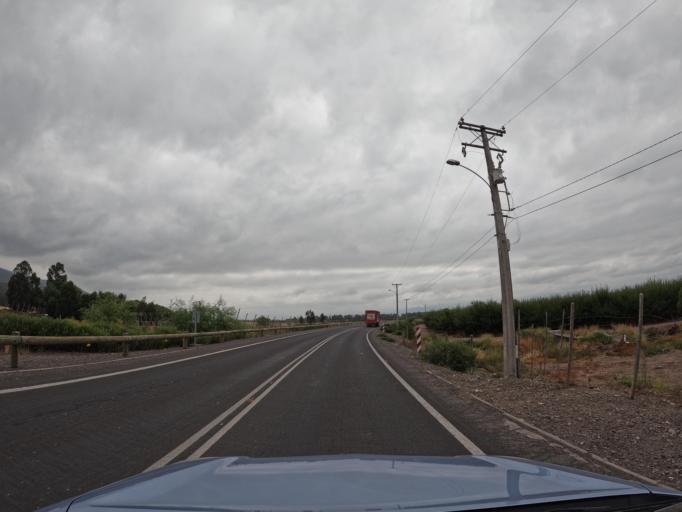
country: CL
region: O'Higgins
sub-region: Provincia de Colchagua
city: Chimbarongo
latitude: -34.7227
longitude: -71.0888
